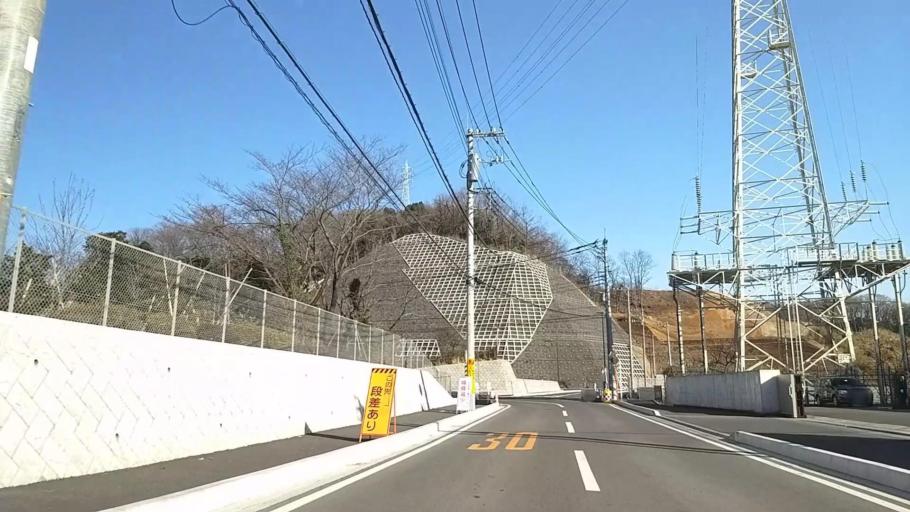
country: JP
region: Kanagawa
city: Atsugi
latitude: 35.4510
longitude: 139.3115
